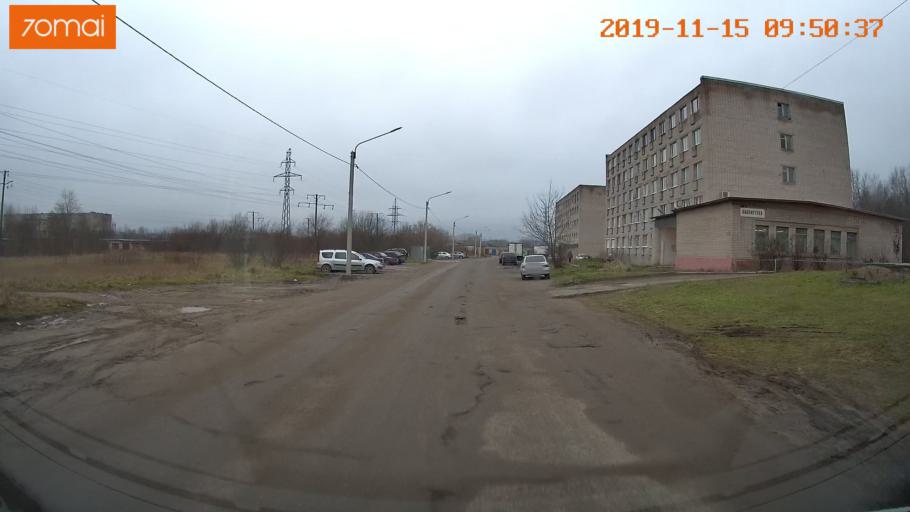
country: RU
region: Vologda
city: Sheksna
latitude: 59.2325
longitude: 38.5108
